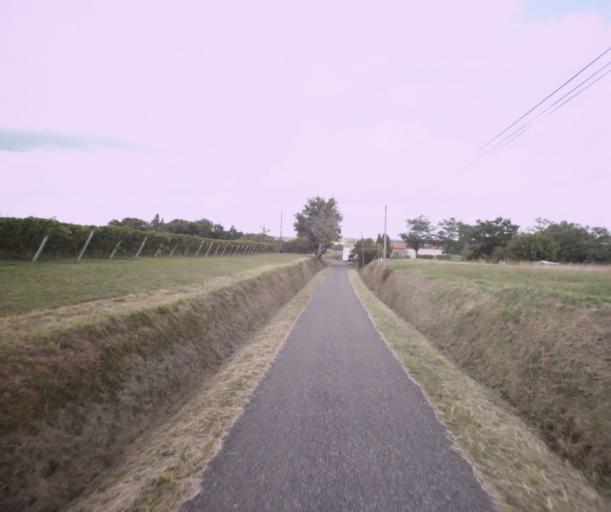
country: FR
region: Midi-Pyrenees
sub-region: Departement du Gers
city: Cazaubon
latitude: 43.8864
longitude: -0.0524
